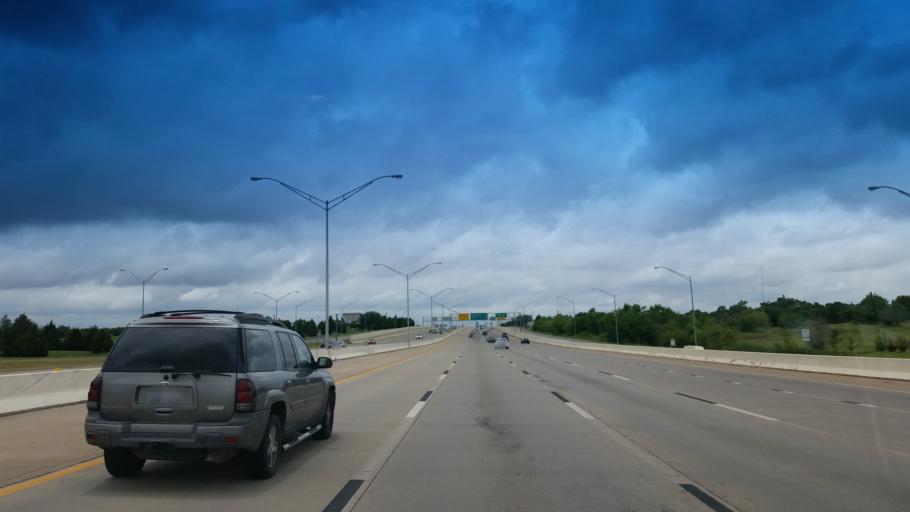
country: US
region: Oklahoma
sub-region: Oklahoma County
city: Nichols Hills
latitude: 35.5622
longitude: -97.5140
